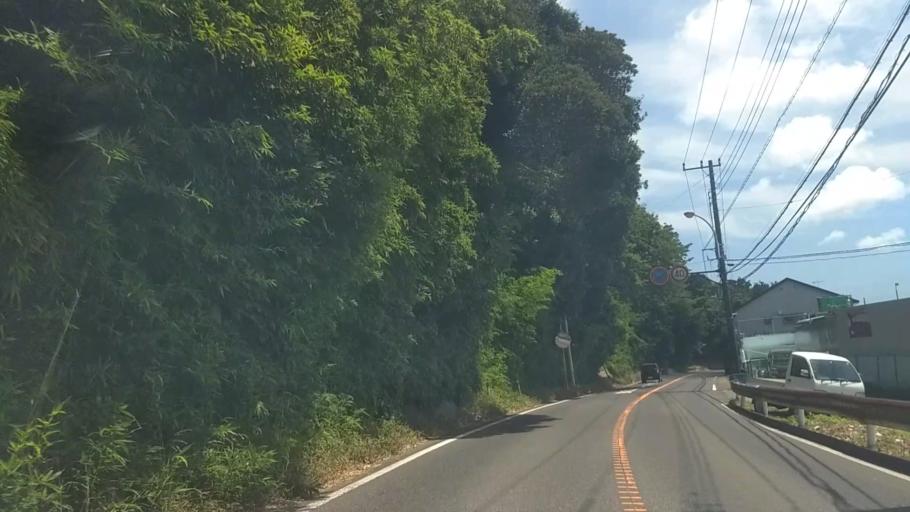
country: JP
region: Kanagawa
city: Miura
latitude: 35.2059
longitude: 139.6484
